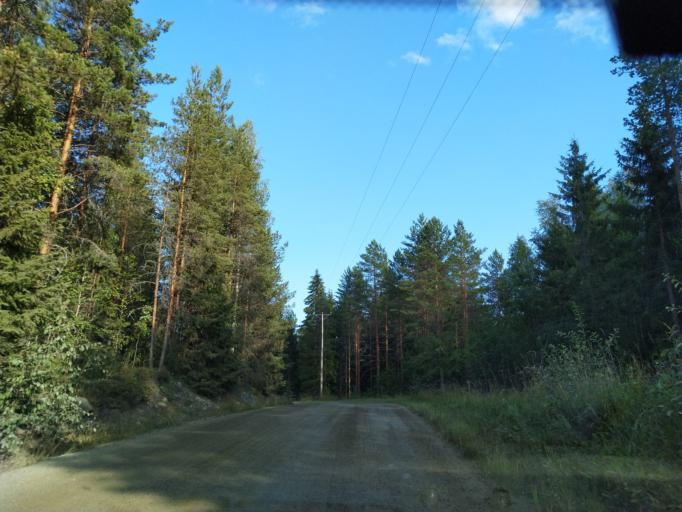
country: FI
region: Central Finland
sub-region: Jaemsae
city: Kuhmoinen
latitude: 61.6900
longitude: 24.9575
